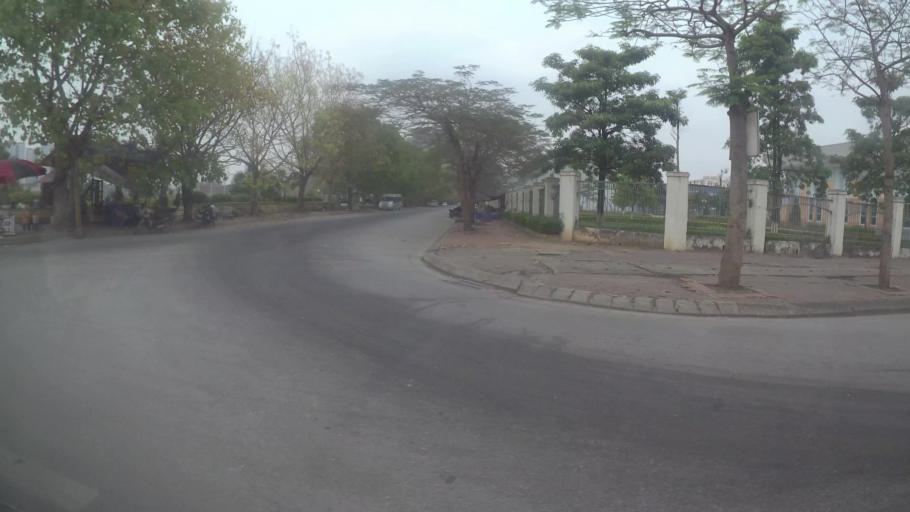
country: VN
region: Ha Noi
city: Cau Dien
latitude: 21.0261
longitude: 105.7601
